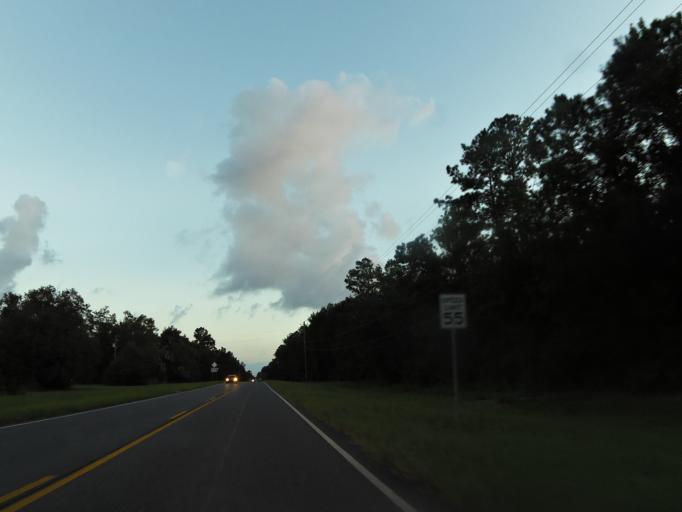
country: US
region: Georgia
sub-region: Camden County
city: Kingsland
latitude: 30.7800
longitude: -81.6867
